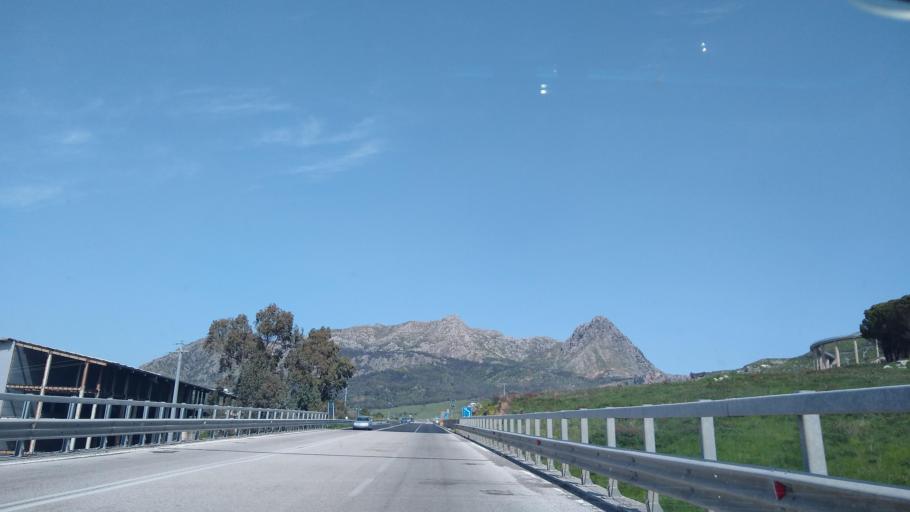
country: IT
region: Sicily
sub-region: Palermo
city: San Giuseppe Jato
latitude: 37.9773
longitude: 13.2175
